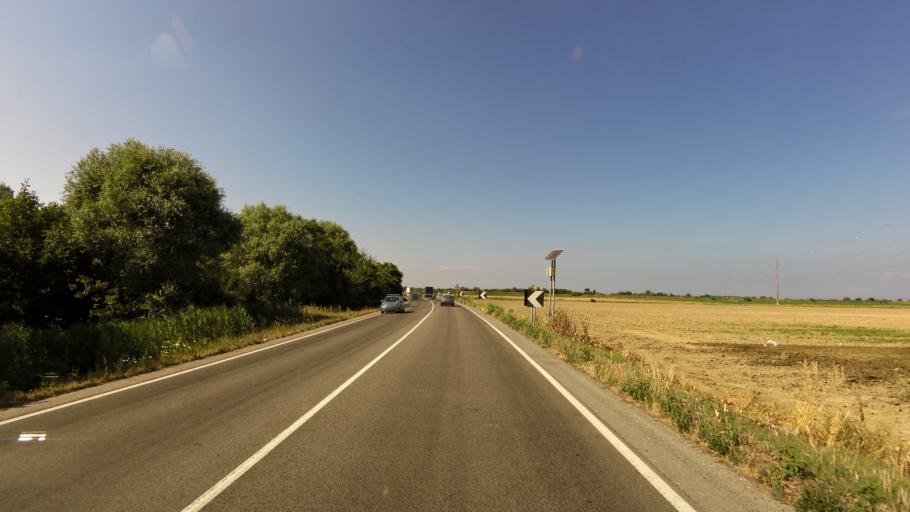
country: IT
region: Emilia-Romagna
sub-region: Provincia di Ravenna
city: Marina Romea
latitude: 44.5740
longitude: 12.2545
